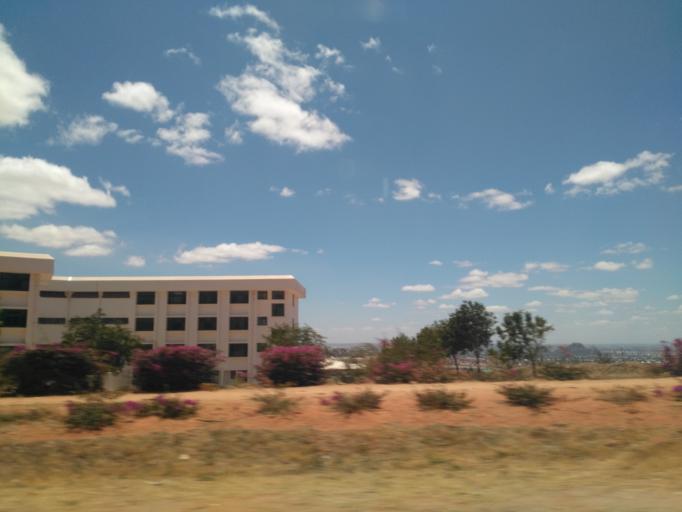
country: TZ
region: Dodoma
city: Kisasa
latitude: -6.2206
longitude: 35.7843
